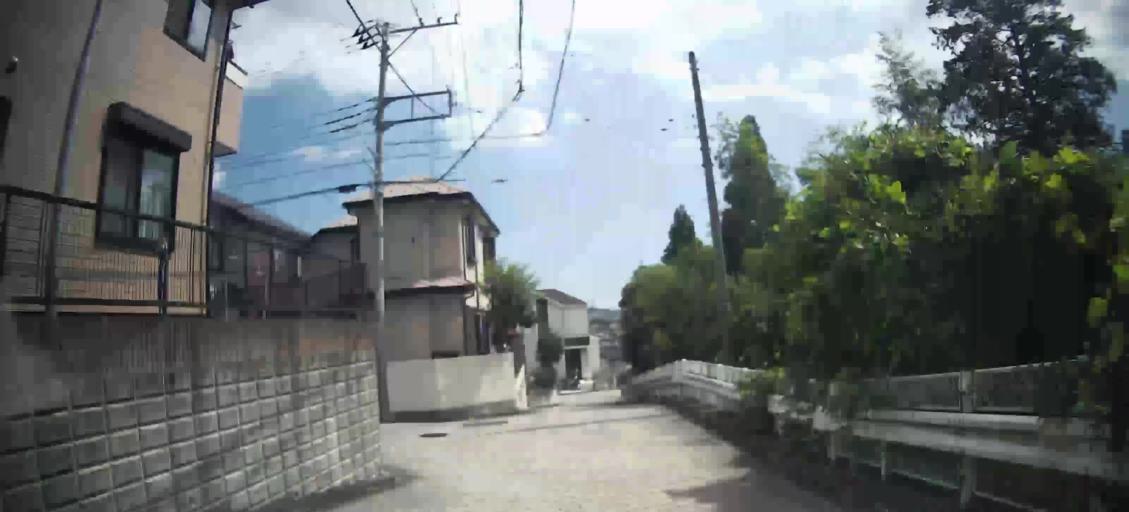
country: JP
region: Kanagawa
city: Yokohama
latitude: 35.4803
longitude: 139.5548
